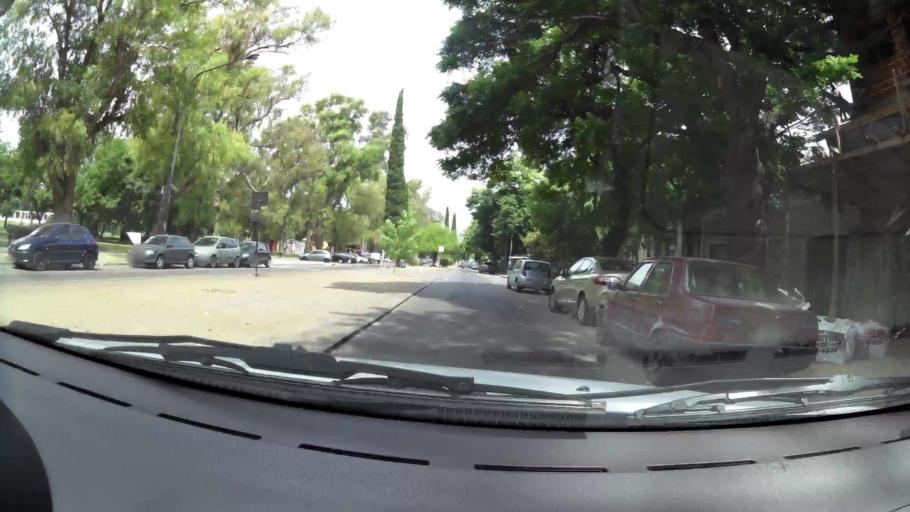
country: AR
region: Buenos Aires
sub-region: Partido de La Plata
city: La Plata
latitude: -34.9315
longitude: -57.9434
